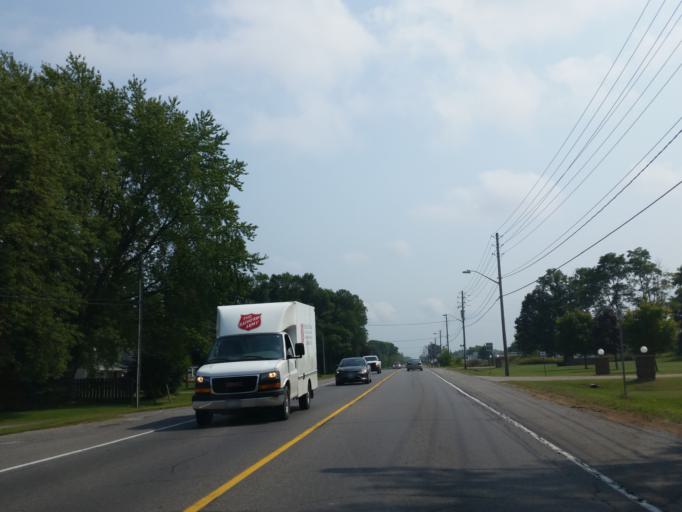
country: CA
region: Ontario
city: Brockville
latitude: 44.6081
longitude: -75.7269
